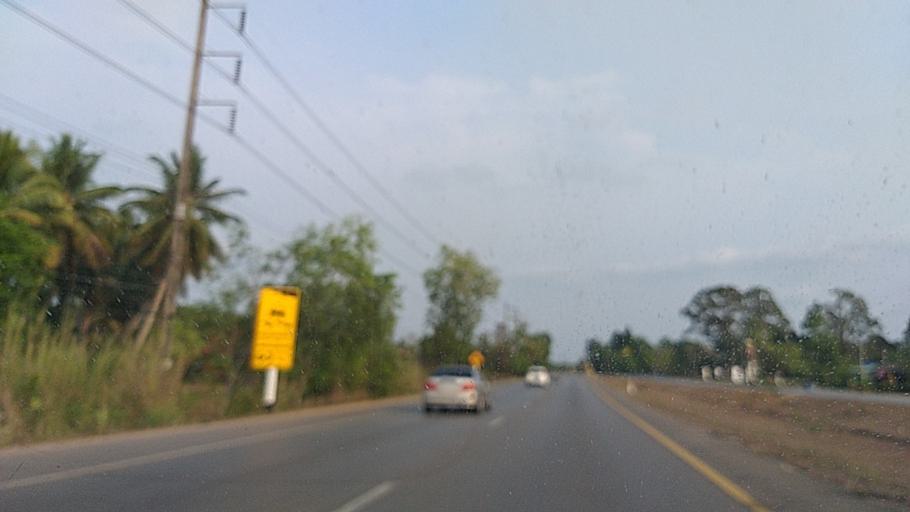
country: TH
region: Trat
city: Khao Saming
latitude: 12.3996
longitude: 102.3479
